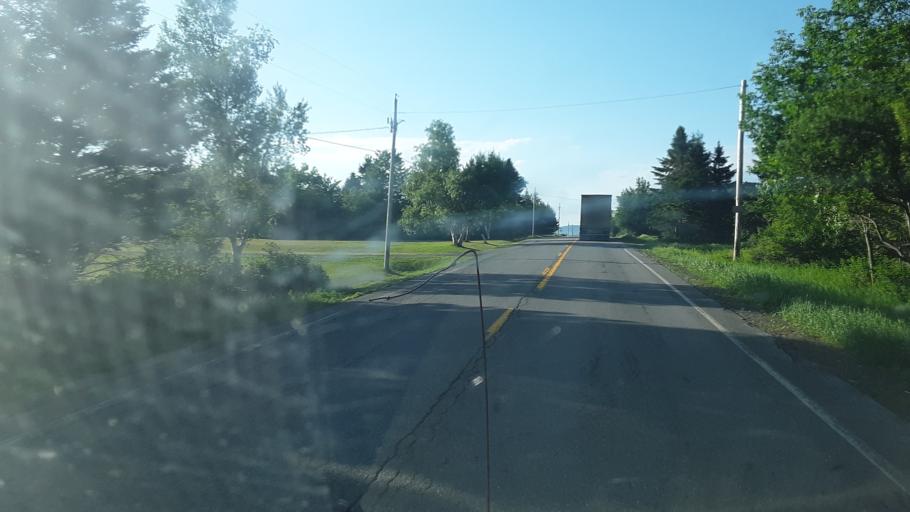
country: US
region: Maine
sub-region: Penobscot County
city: Patten
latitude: 46.1728
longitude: -68.2393
